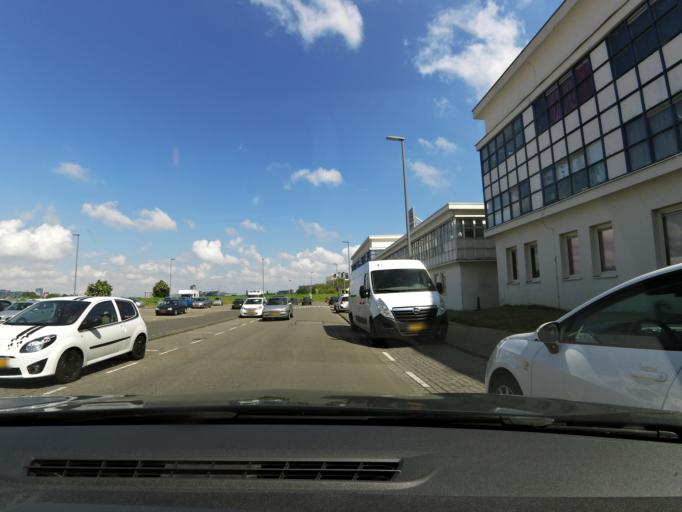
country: NL
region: South Holland
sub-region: Gemeente Rotterdam
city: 's-Gravenland
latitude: 51.9106
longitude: 4.5196
